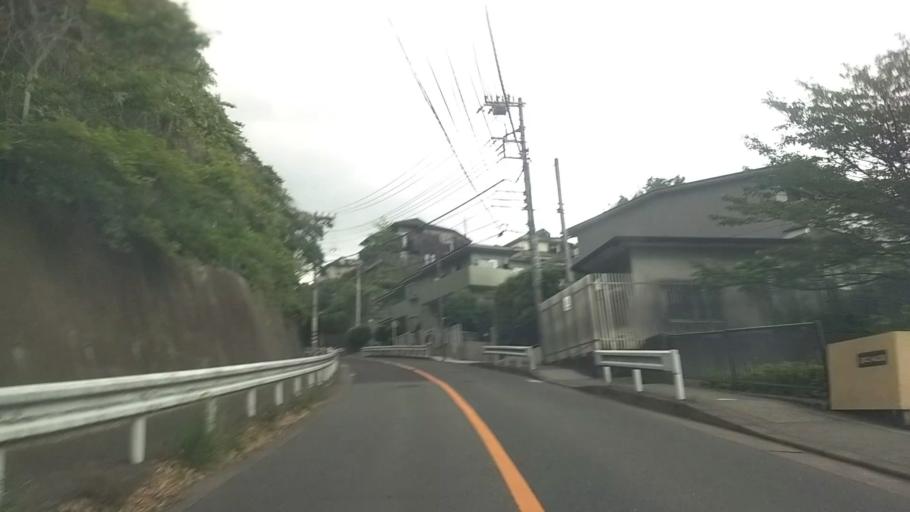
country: JP
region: Kanagawa
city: Kamakura
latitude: 35.3556
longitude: 139.5226
